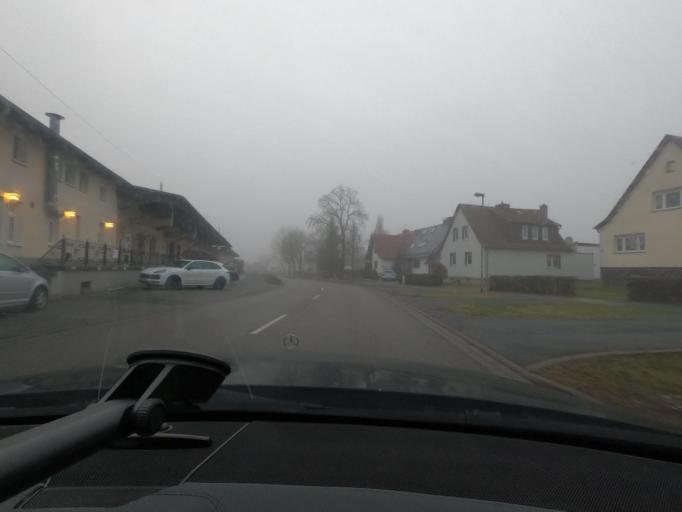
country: DE
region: Thuringia
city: Leinefelde
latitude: 51.3892
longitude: 10.3303
